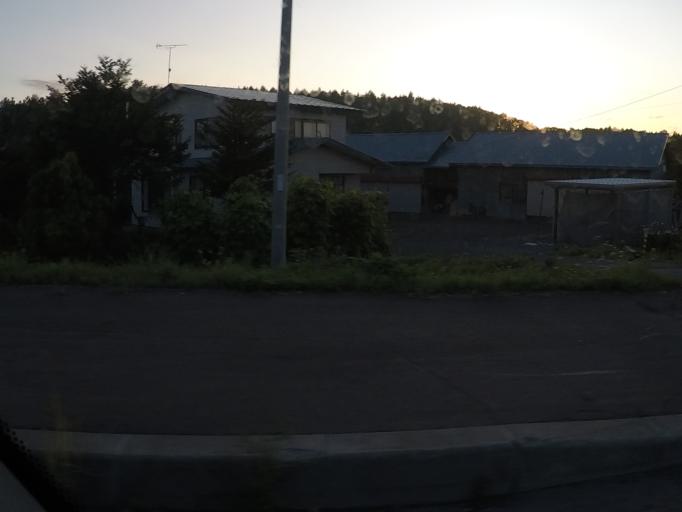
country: JP
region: Hokkaido
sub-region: Asahikawa-shi
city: Asahikawa
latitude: 43.6168
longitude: 142.4764
